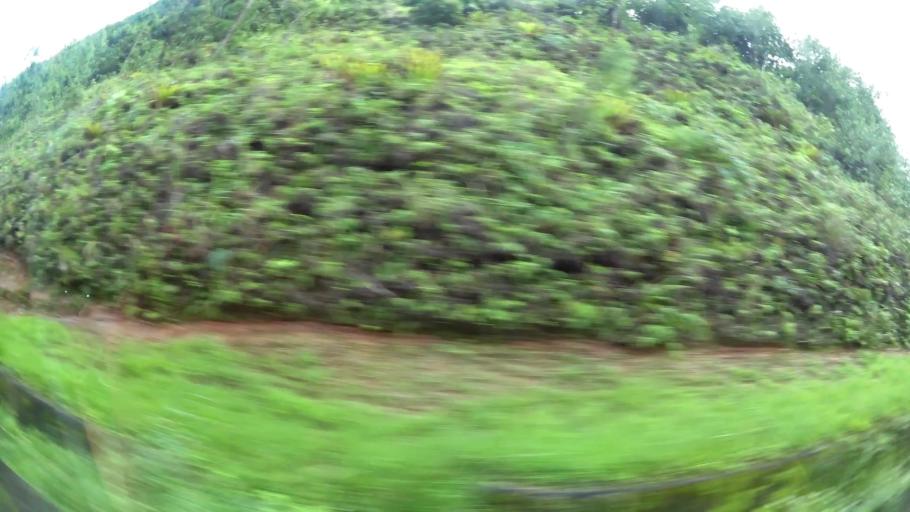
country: GP
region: Guadeloupe
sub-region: Guadeloupe
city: Bouillante
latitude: 16.1803
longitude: -61.7280
